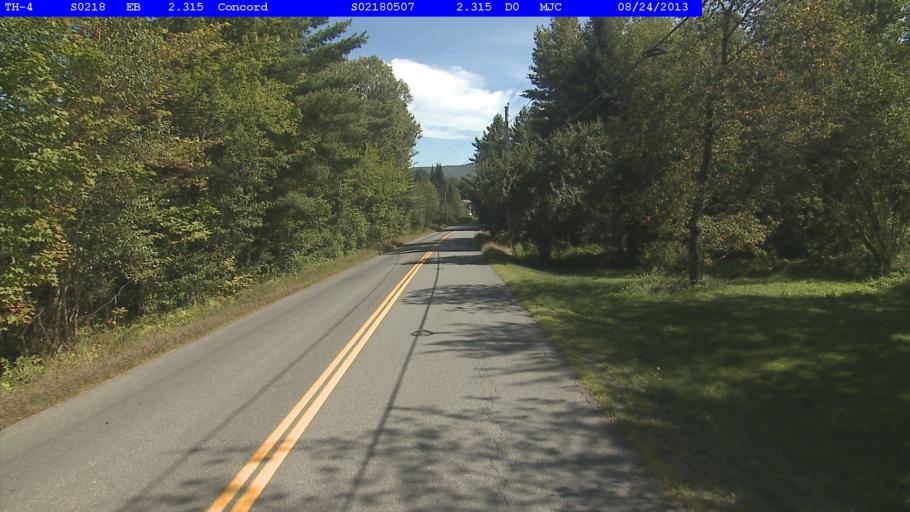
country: US
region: New Hampshire
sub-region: Grafton County
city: Littleton
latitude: 44.4348
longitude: -71.7565
